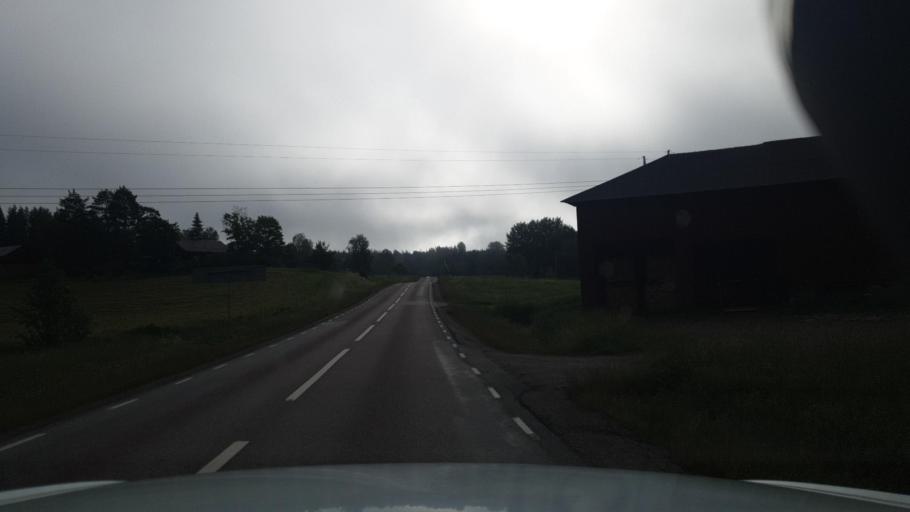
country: SE
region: Vaermland
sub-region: Sunne Kommun
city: Sunne
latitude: 59.6569
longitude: 12.9510
